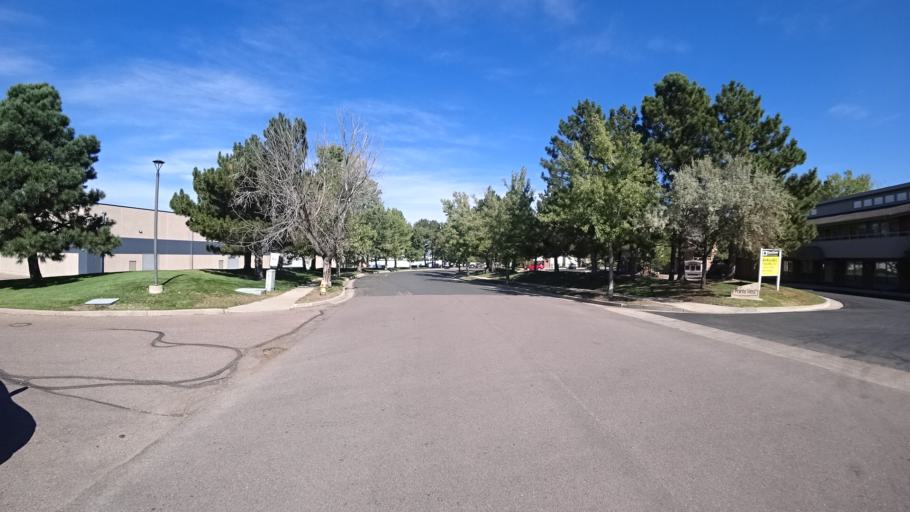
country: US
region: Colorado
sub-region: El Paso County
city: Colorado Springs
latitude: 38.9114
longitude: -104.7852
